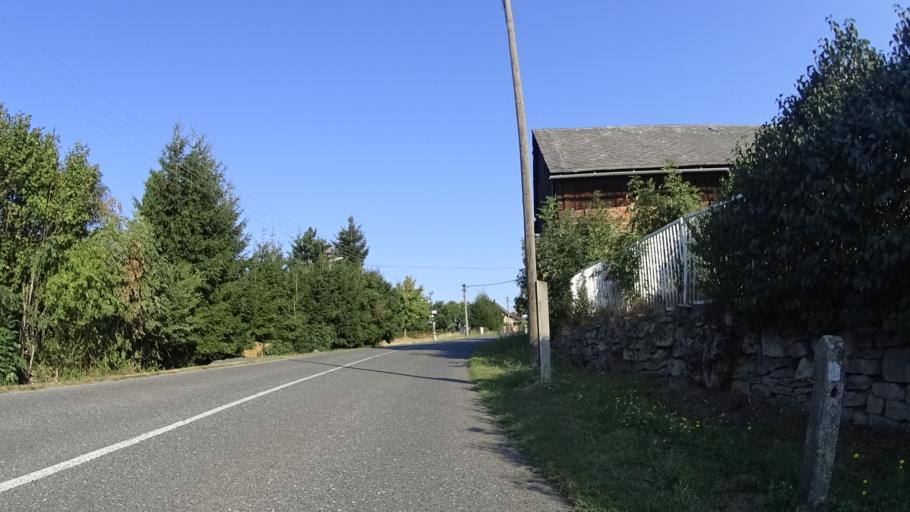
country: CZ
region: Liberecky
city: Hodkovice nad Mohelkou
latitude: 50.6408
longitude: 15.1109
